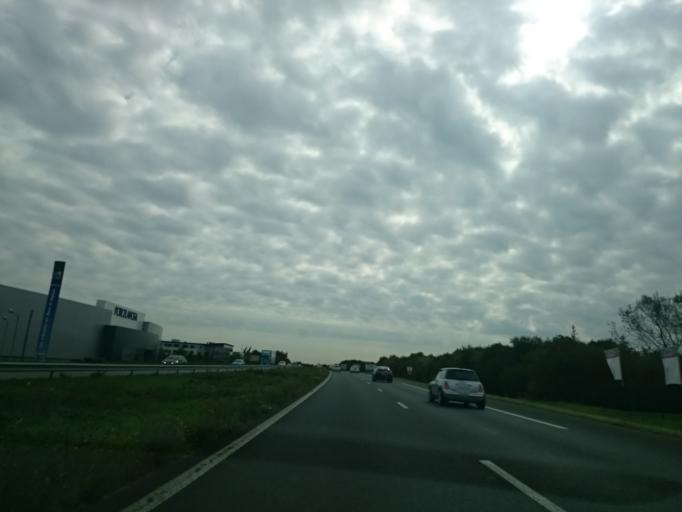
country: FR
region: Pays de la Loire
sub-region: Departement de la Loire-Atlantique
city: Saint-Herblain
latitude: 47.2383
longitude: -1.6620
